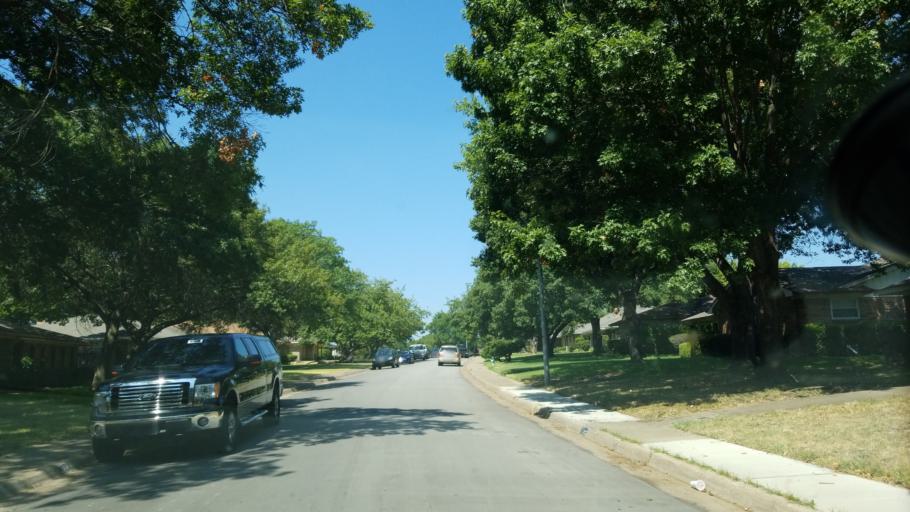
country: US
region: Texas
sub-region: Dallas County
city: Duncanville
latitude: 32.6541
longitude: -96.8937
